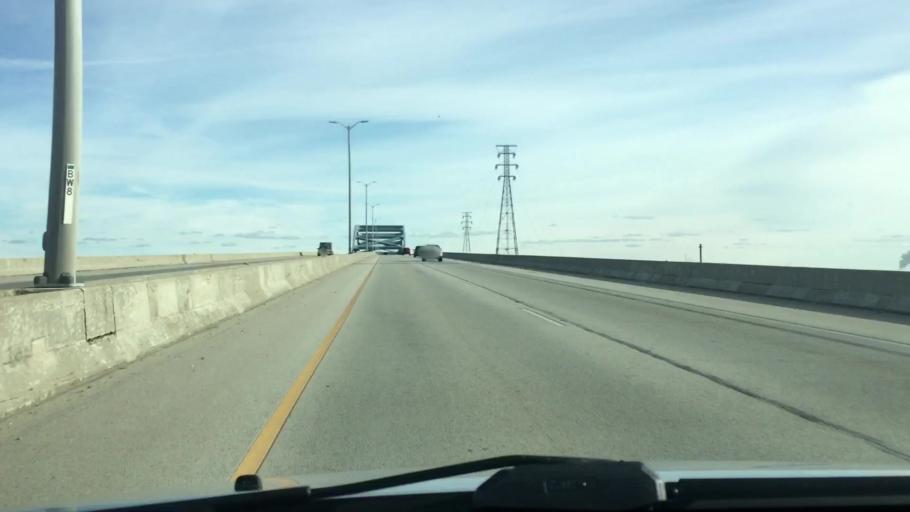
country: US
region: Wisconsin
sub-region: Brown County
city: Green Bay
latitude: 44.5353
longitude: -88.0143
